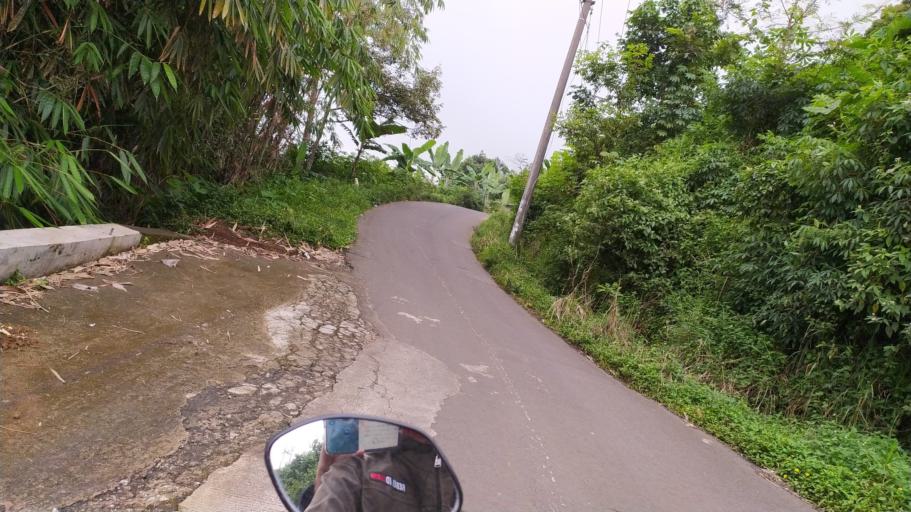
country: ID
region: West Java
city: Ciampea
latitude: -6.6451
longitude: 106.7047
